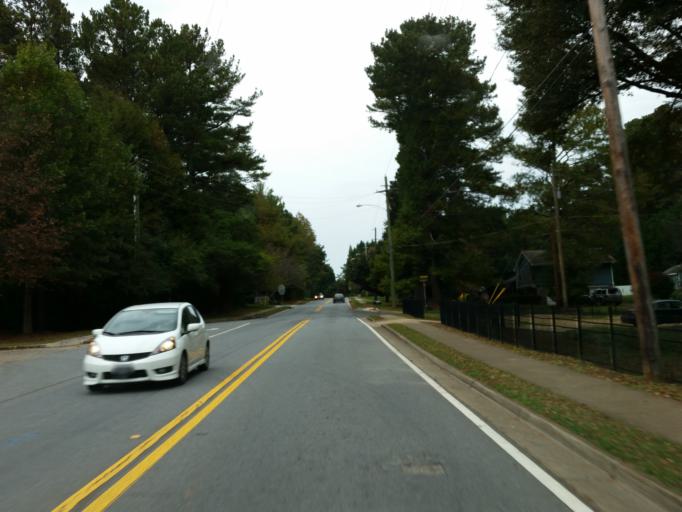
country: US
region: Georgia
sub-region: Cherokee County
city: Woodstock
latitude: 34.0342
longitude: -84.4808
